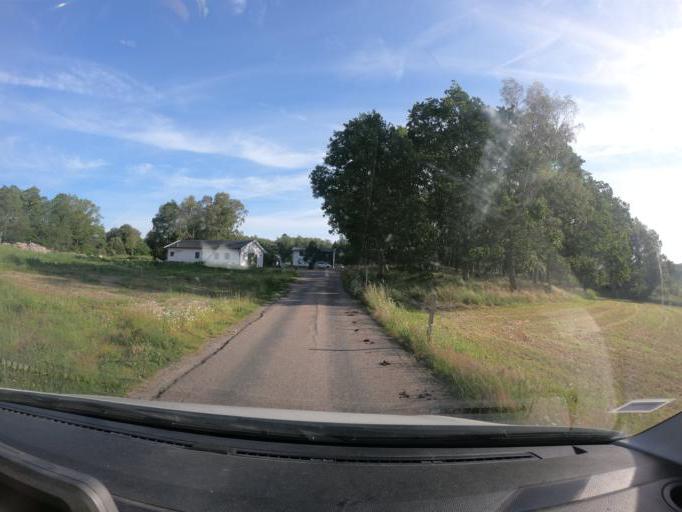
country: SE
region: Skane
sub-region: Angelholms Kommun
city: Munka-Ljungby
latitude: 56.3291
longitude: 12.9758
